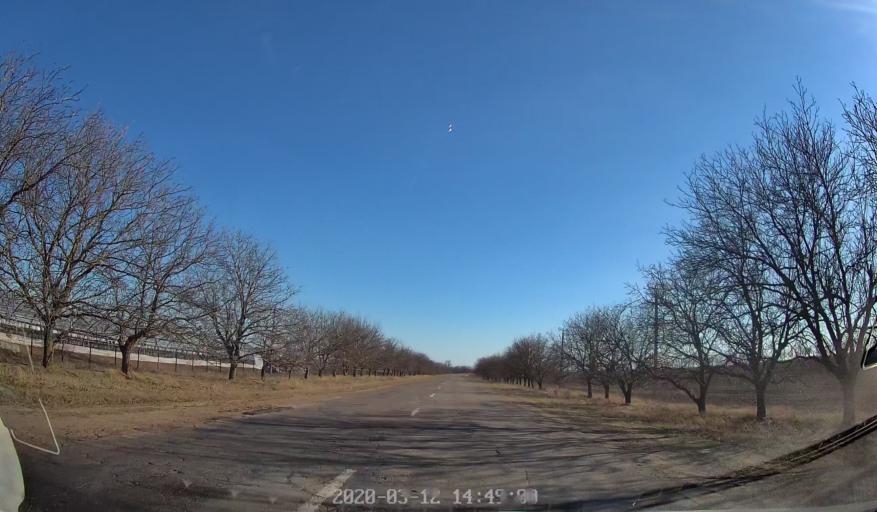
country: MD
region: Criuleni
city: Criuleni
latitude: 47.2276
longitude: 29.1428
